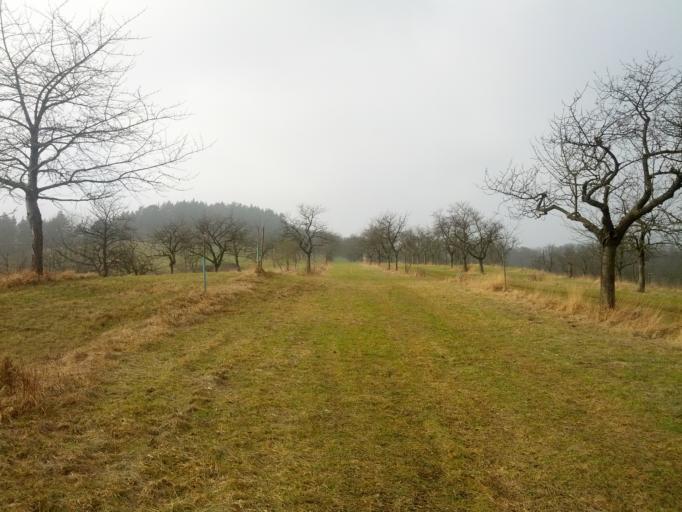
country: DE
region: Thuringia
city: Treffurt
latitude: 51.1426
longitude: 10.2361
